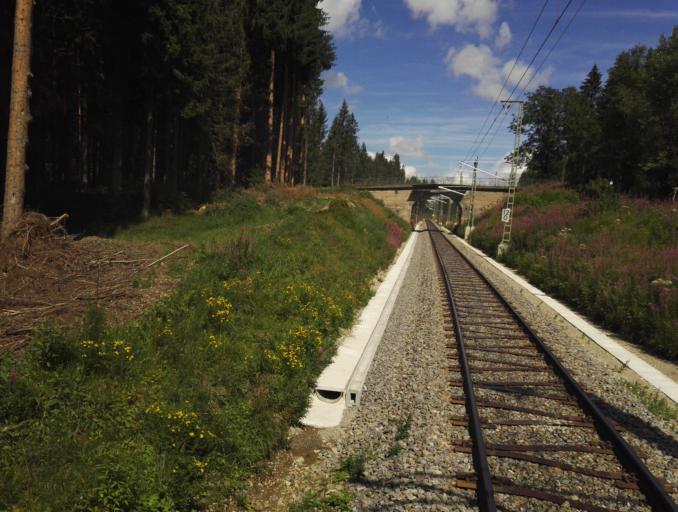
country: DE
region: Baden-Wuerttemberg
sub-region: Freiburg Region
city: Schluchsee
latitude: 47.8440
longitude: 8.1295
